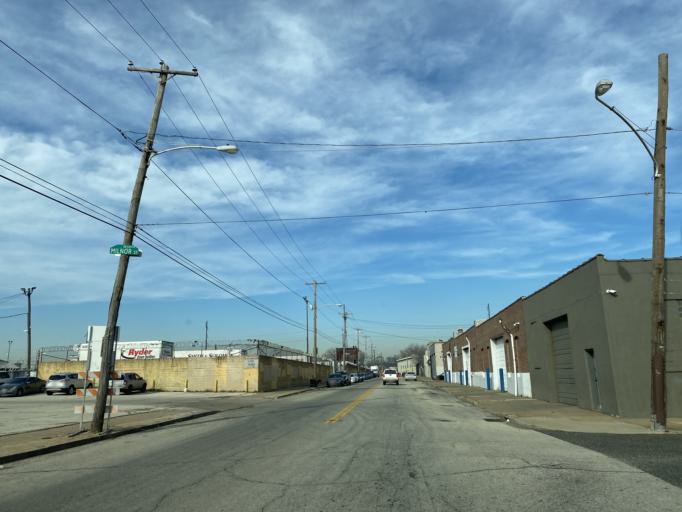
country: US
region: New Jersey
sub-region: Burlington County
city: Palmyra
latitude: 40.0047
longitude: -75.0824
